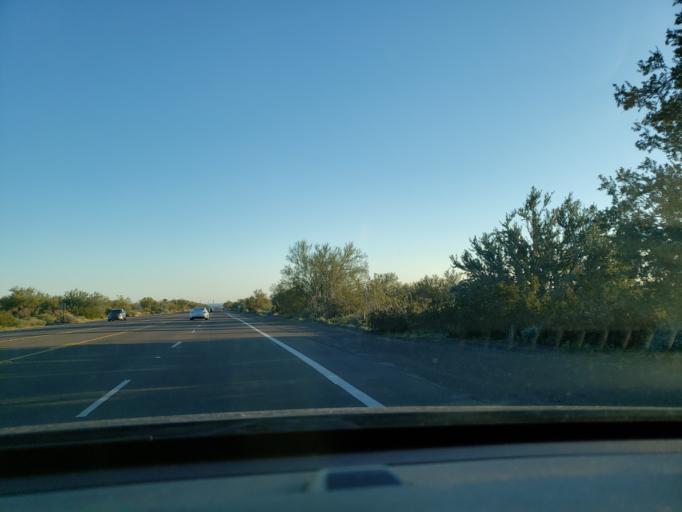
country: US
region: Arizona
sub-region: Maricopa County
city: Carefree
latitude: 33.7095
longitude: -111.9255
